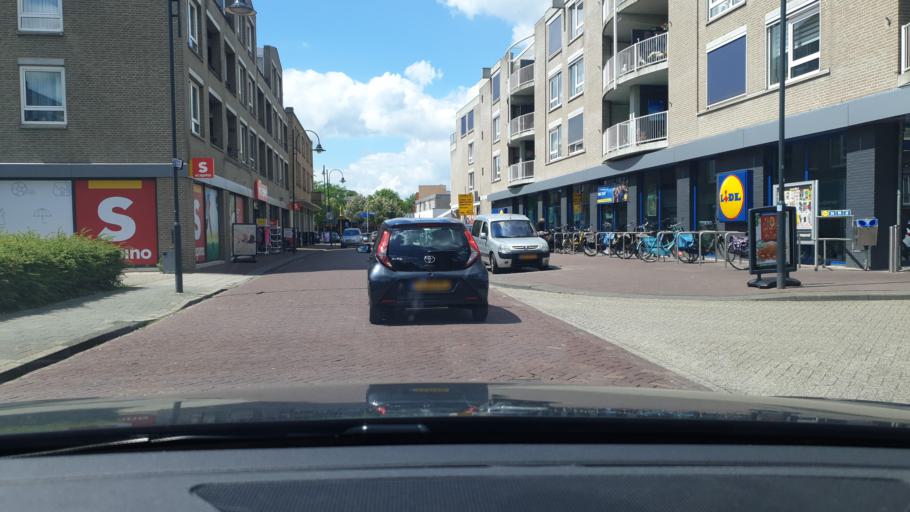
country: NL
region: North Brabant
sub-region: Gemeente Veghel
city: Veghel
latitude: 51.6169
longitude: 5.5478
